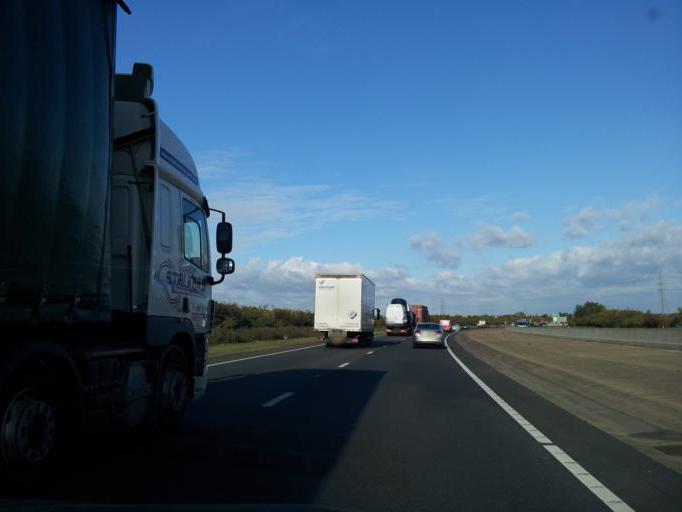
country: GB
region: England
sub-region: Central Bedfordshire
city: Marston Moretaine
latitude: 52.0614
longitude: -0.5682
